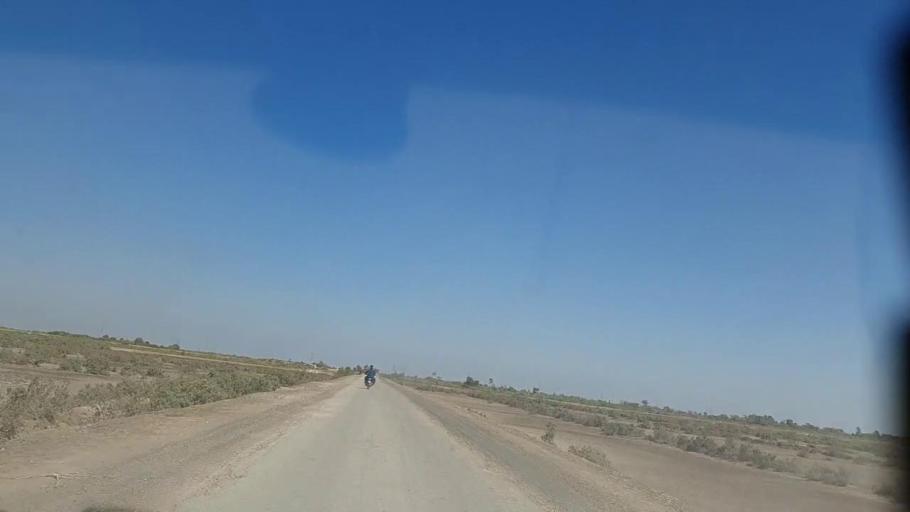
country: PK
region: Sindh
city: Mirwah Gorchani
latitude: 25.2438
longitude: 69.0320
